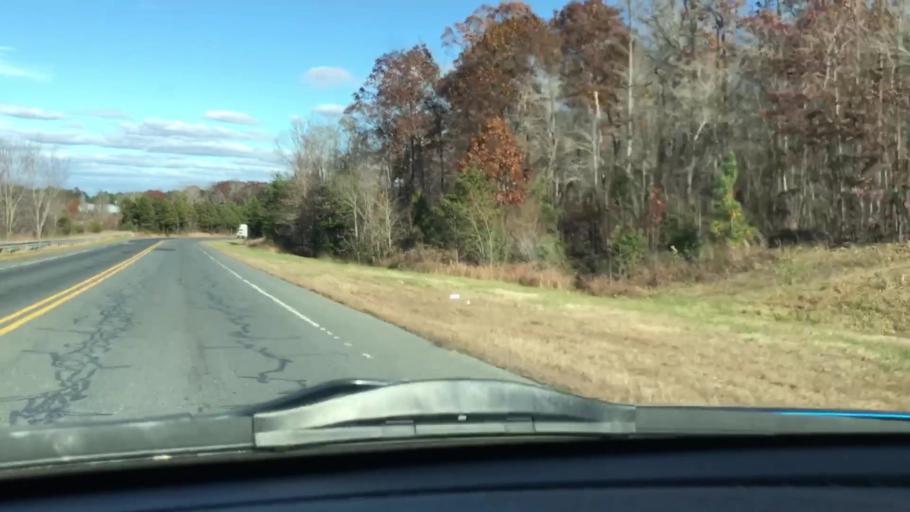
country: US
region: North Carolina
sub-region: Randolph County
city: Asheboro
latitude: 35.7175
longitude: -79.7797
